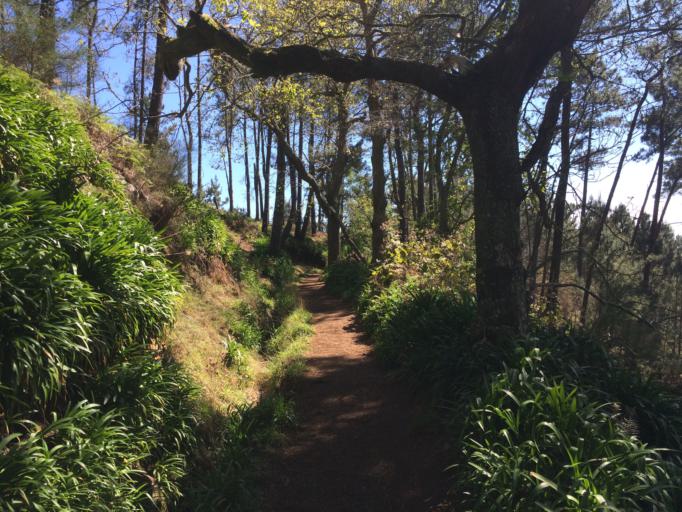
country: PT
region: Madeira
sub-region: Santa Cruz
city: Camacha
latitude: 32.6775
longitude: -16.8567
